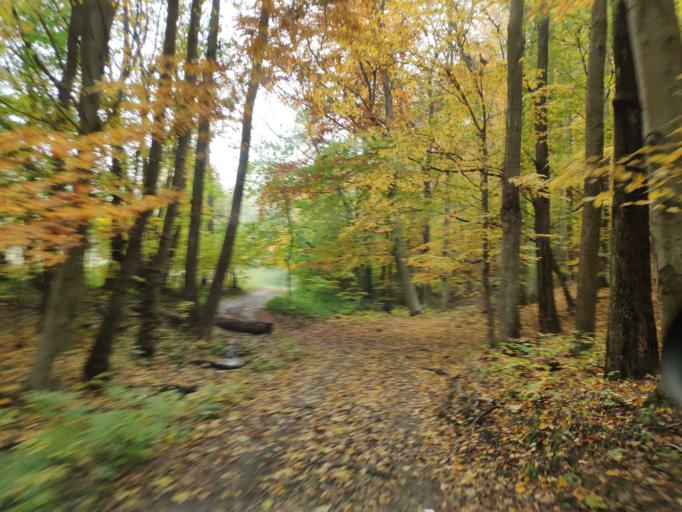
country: SK
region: Kosicky
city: Moldava nad Bodvou
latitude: 48.7188
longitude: 21.0100
